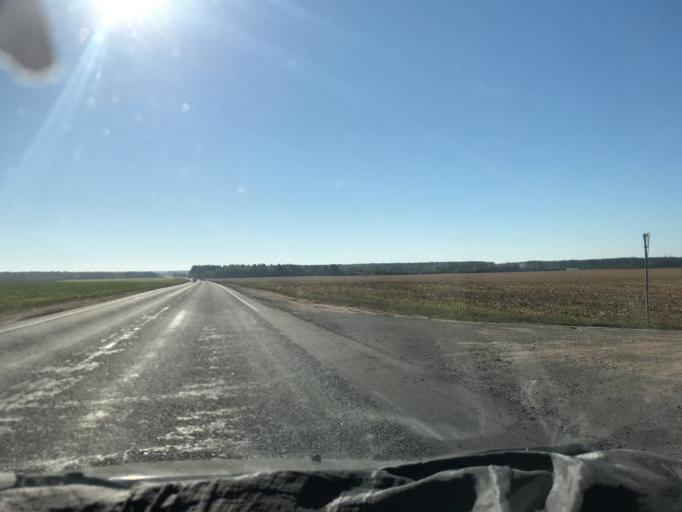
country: BY
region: Mogilev
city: Babruysk
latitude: 53.0967
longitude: 29.0591
